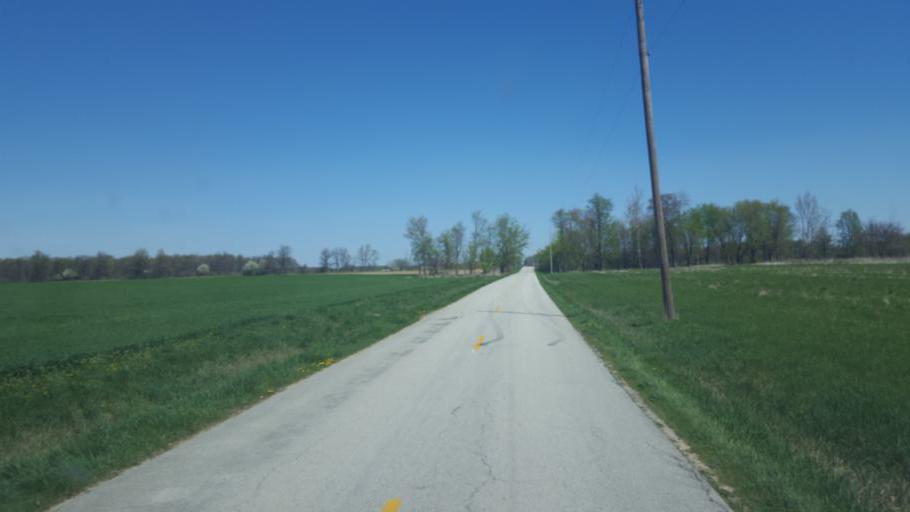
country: US
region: Ohio
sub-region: Ottawa County
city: Oak Harbor
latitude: 41.4545
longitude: -83.1258
